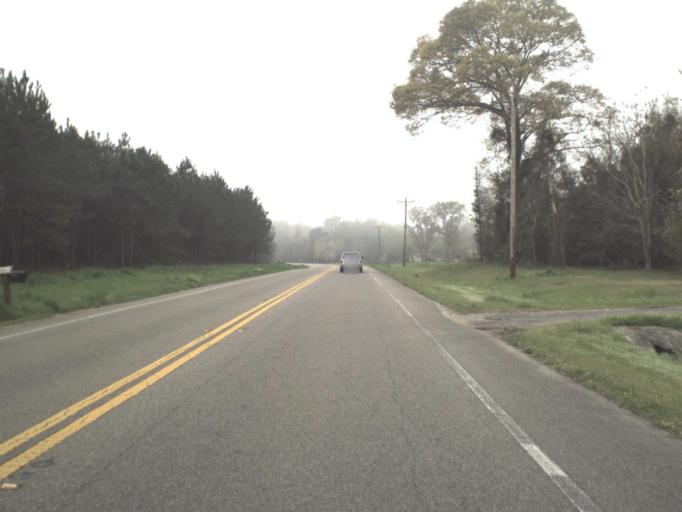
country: US
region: Florida
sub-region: Gadsden County
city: Gretna
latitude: 30.5384
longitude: -84.6801
